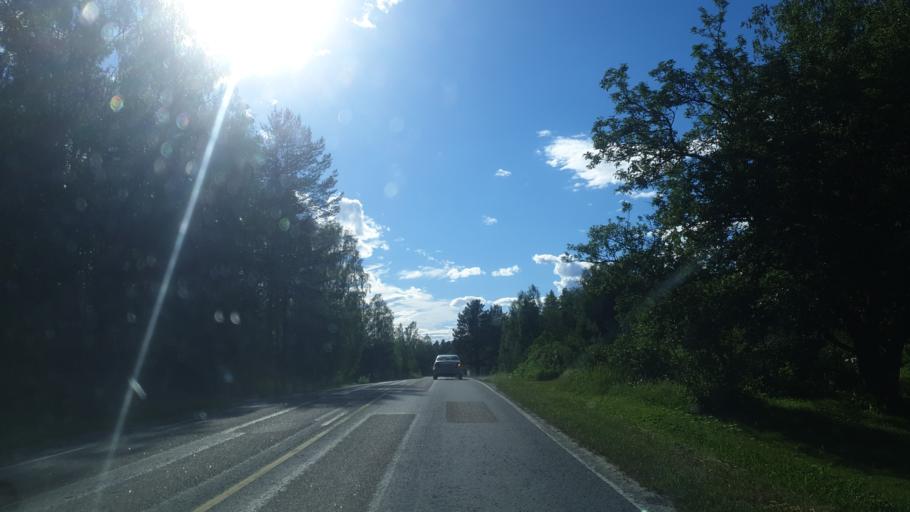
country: FI
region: Southern Savonia
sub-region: Mikkeli
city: Pertunmaa
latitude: 61.5230
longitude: 26.5518
